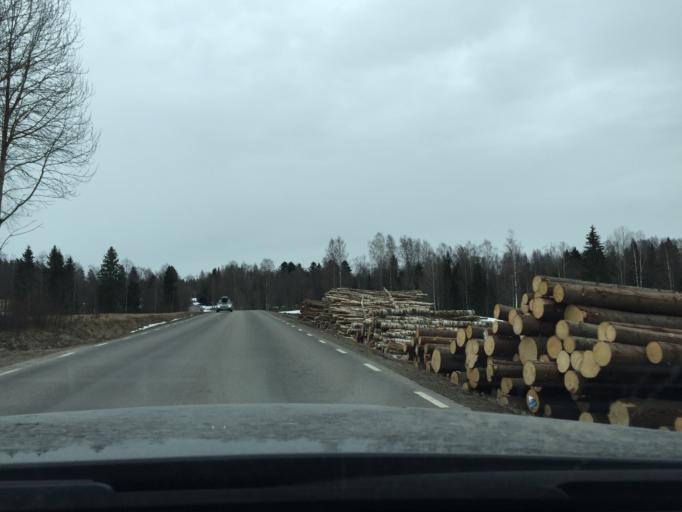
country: SE
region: Gaevleborg
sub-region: Sandvikens Kommun
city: Jarbo
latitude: 60.7611
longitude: 16.5279
